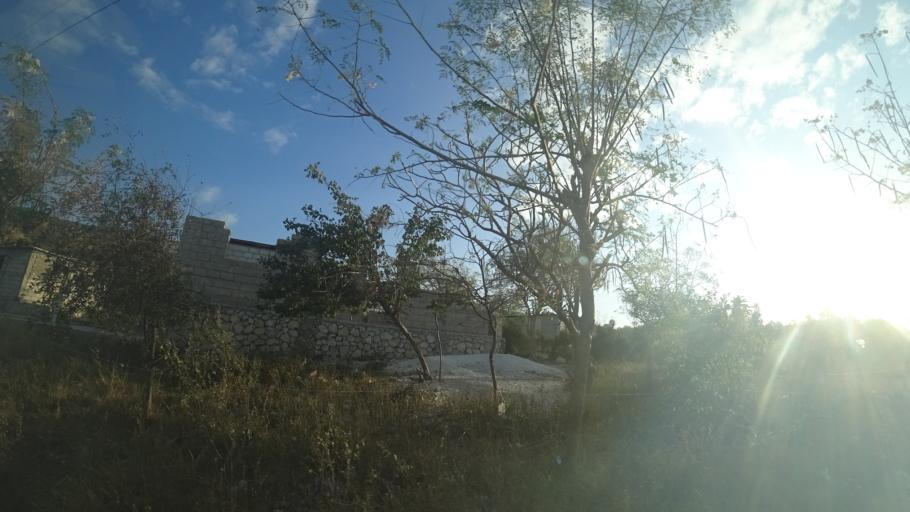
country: HT
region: Ouest
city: Croix des Bouquets
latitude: 18.6697
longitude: -72.2811
